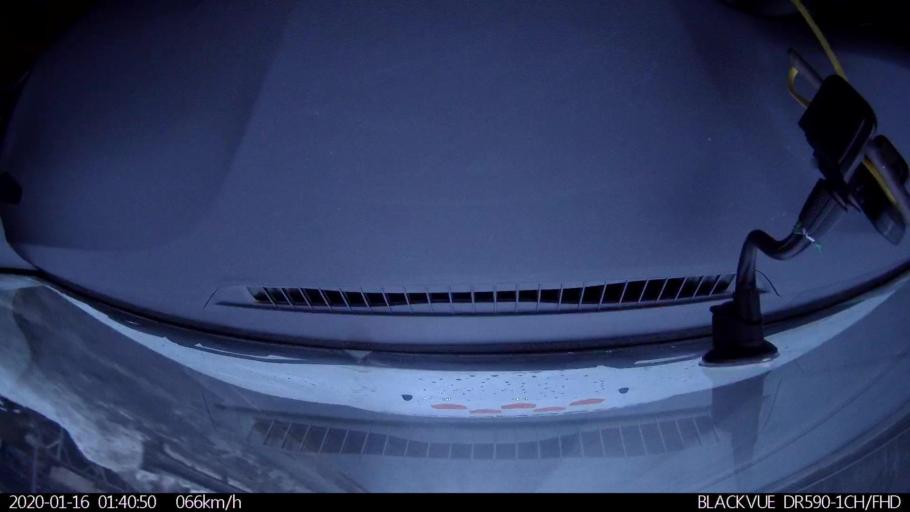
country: RU
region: Nizjnij Novgorod
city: Gorbatovka
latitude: 56.3229
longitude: 43.7758
